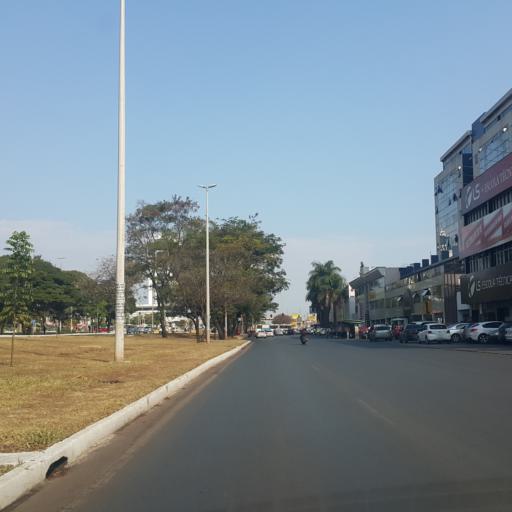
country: BR
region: Federal District
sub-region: Brasilia
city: Brasilia
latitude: -15.8401
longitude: -48.0471
